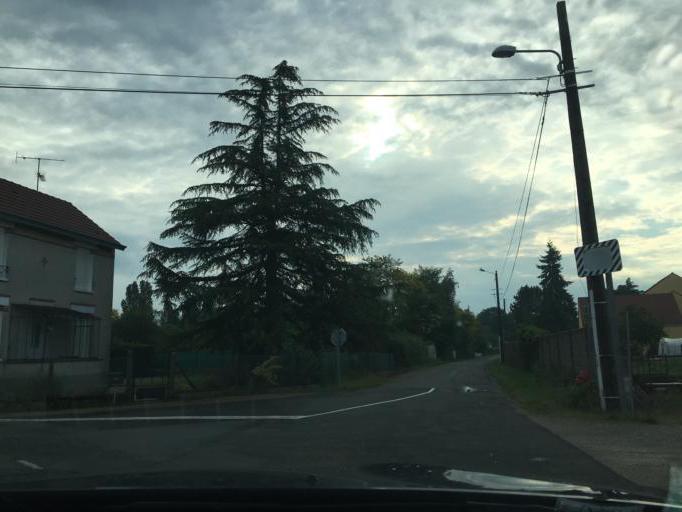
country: FR
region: Centre
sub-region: Departement du Loiret
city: Saint-Denis-en-Val
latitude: 47.8921
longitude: 1.9522
